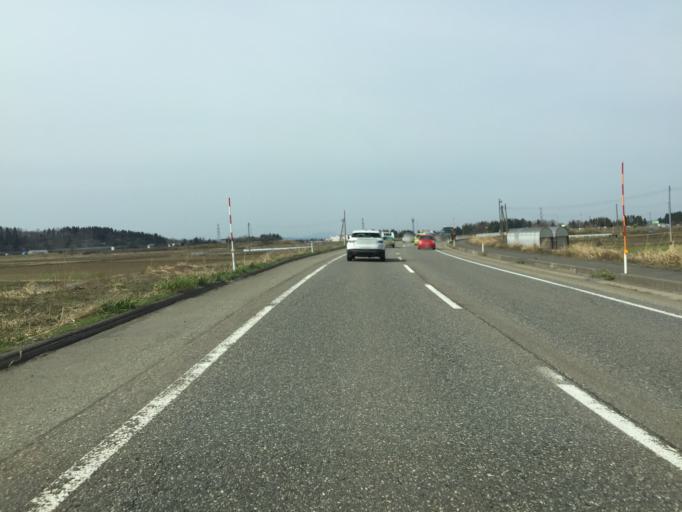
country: JP
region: Niigata
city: Ojiya
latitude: 37.3355
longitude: 138.8115
